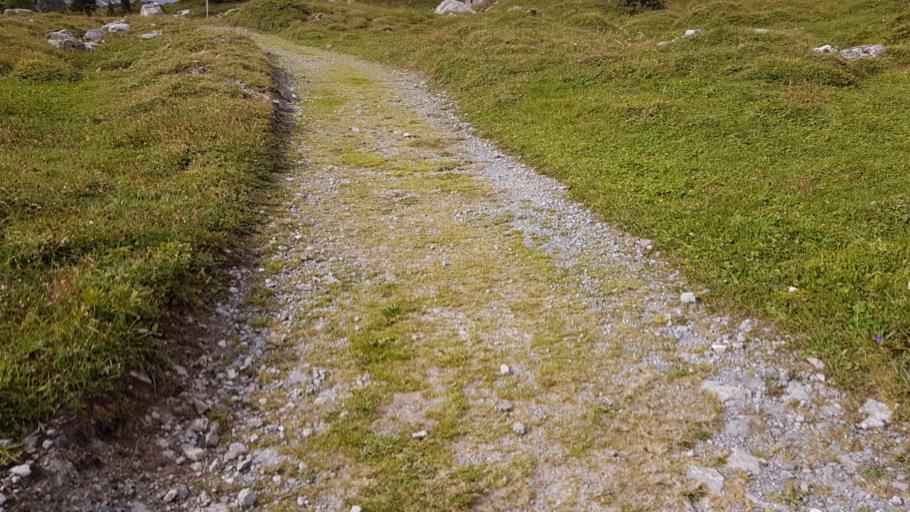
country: CH
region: Bern
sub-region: Frutigen-Niedersimmental District
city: Kandersteg
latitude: 46.4565
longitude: 7.6467
